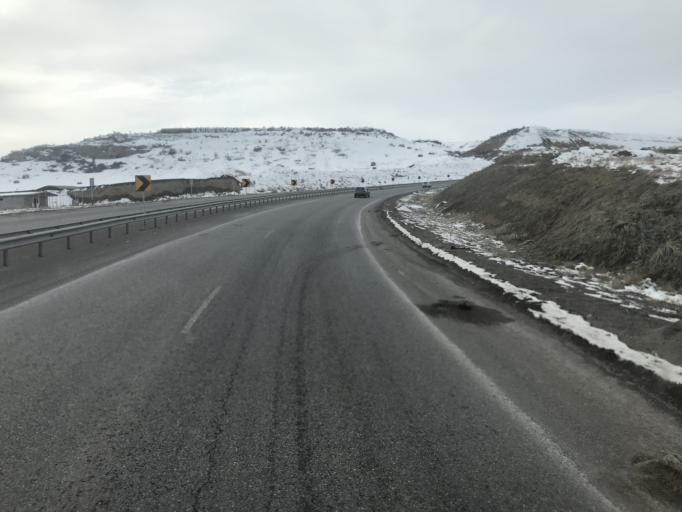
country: KZ
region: Ongtustik Qazaqstan
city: Sastobe
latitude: 42.4935
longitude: 69.9589
